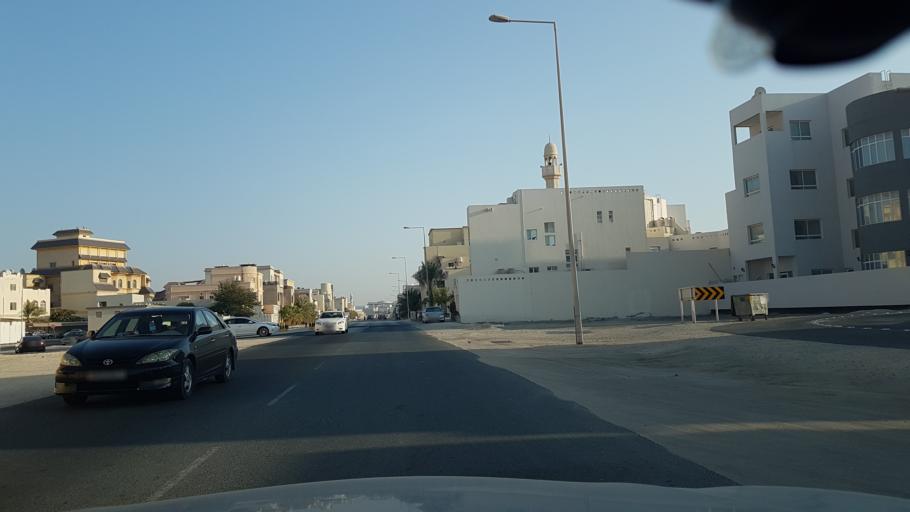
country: BH
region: Muharraq
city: Al Muharraq
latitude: 26.2777
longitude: 50.6030
